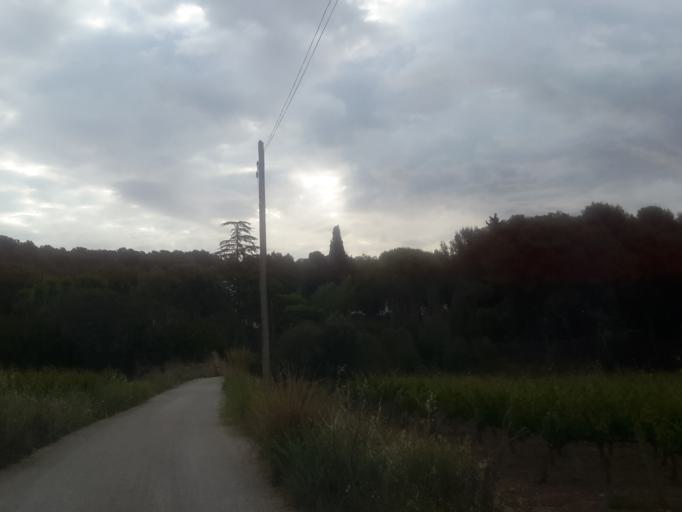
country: ES
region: Catalonia
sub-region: Provincia de Barcelona
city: Vilanova i la Geltru
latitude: 41.2514
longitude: 1.7346
